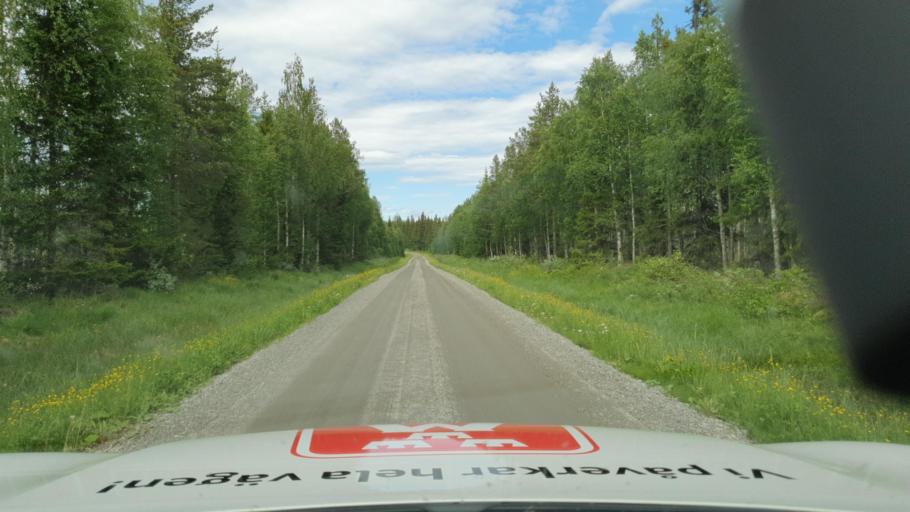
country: SE
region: Vaesterbotten
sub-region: Norsjo Kommun
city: Norsjoe
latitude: 64.7890
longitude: 19.6607
